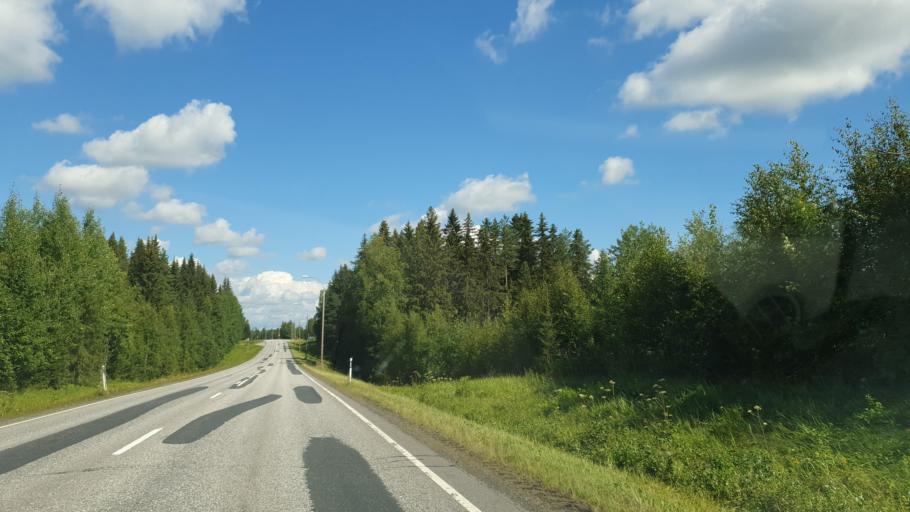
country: FI
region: Northern Savo
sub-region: Ylae-Savo
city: Sonkajaervi
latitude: 63.7225
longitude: 27.3699
